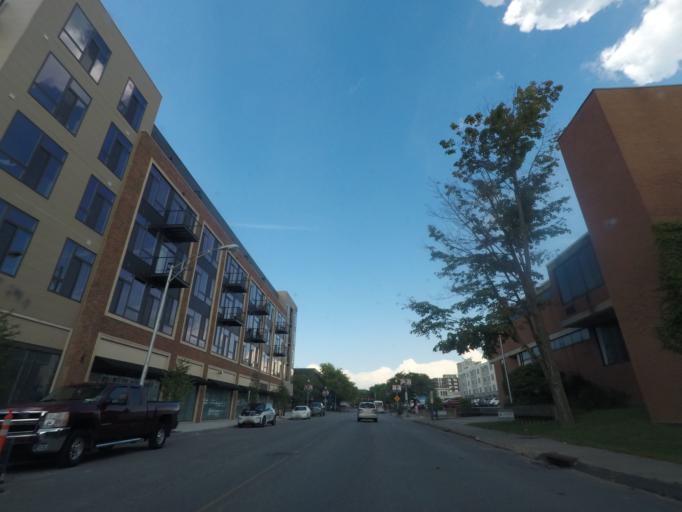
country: US
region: New York
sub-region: Rensselaer County
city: Troy
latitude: 42.7302
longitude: -73.6867
